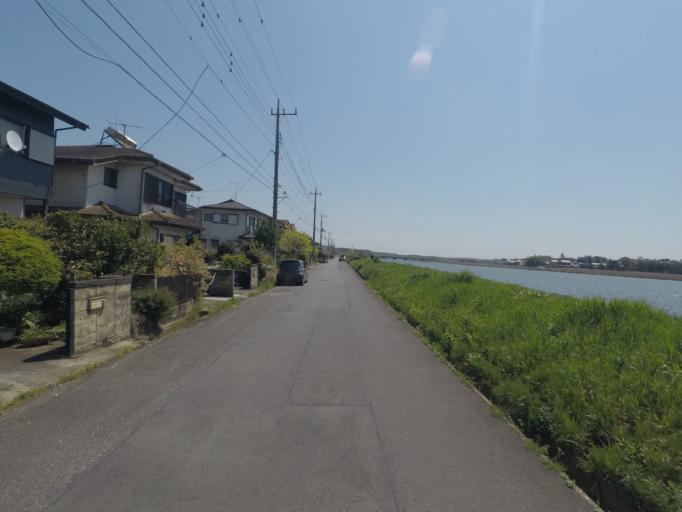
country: JP
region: Ibaraki
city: Ushiku
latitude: 35.9932
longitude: 140.1042
